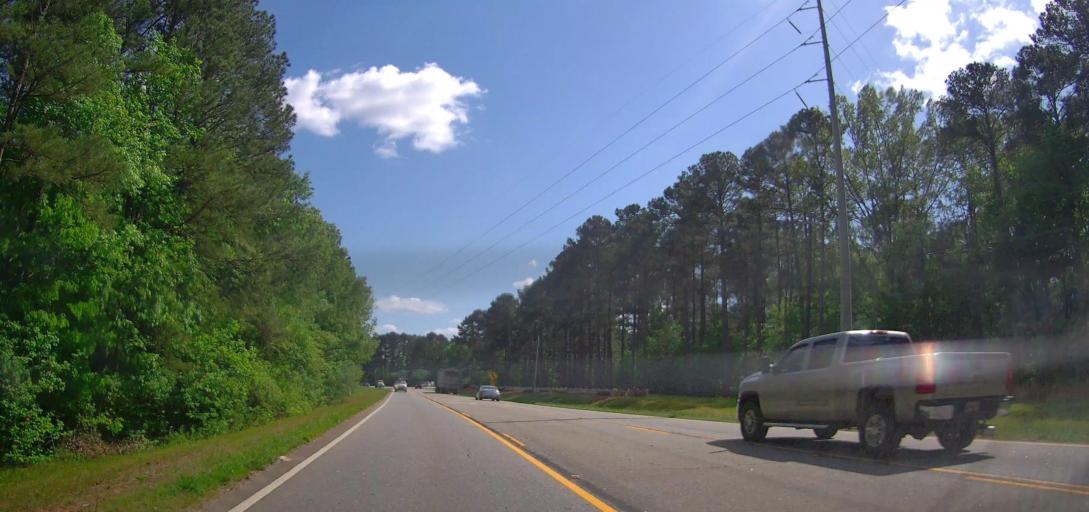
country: US
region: Georgia
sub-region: Putnam County
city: Jefferson
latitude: 33.4725
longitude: -83.2457
